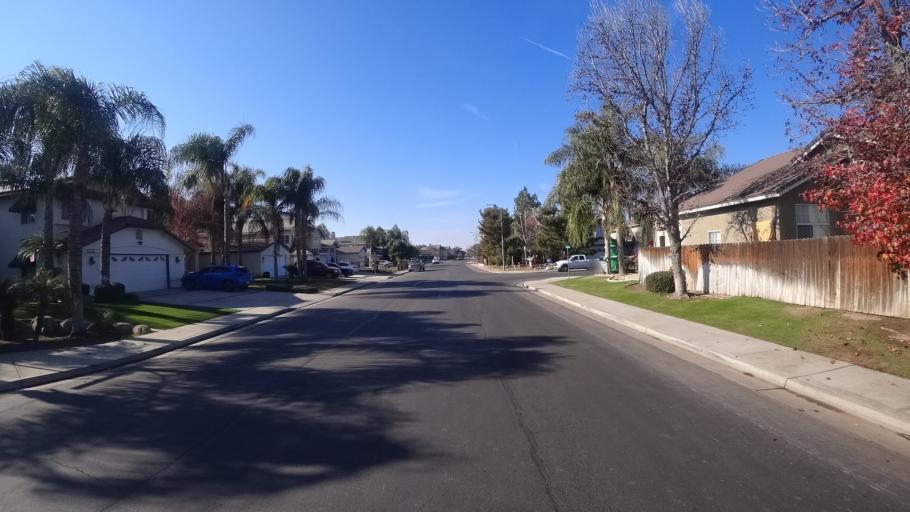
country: US
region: California
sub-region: Kern County
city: Greenacres
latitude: 35.3196
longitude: -119.1226
